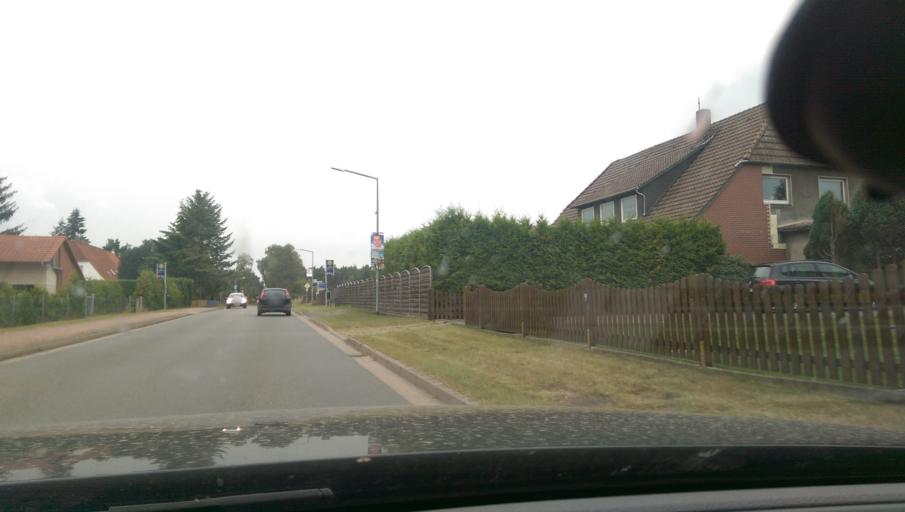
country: DE
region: Lower Saxony
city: Hagenburg
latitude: 52.4871
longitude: 9.2805
